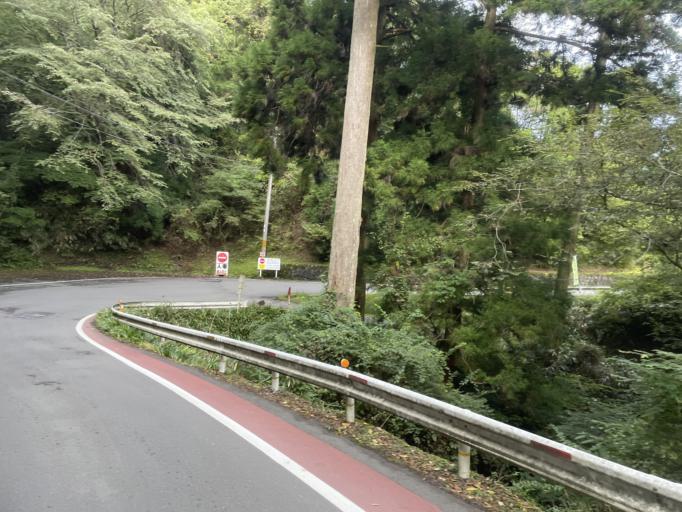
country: JP
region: Wakayama
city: Koya
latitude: 34.2206
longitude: 135.5800
